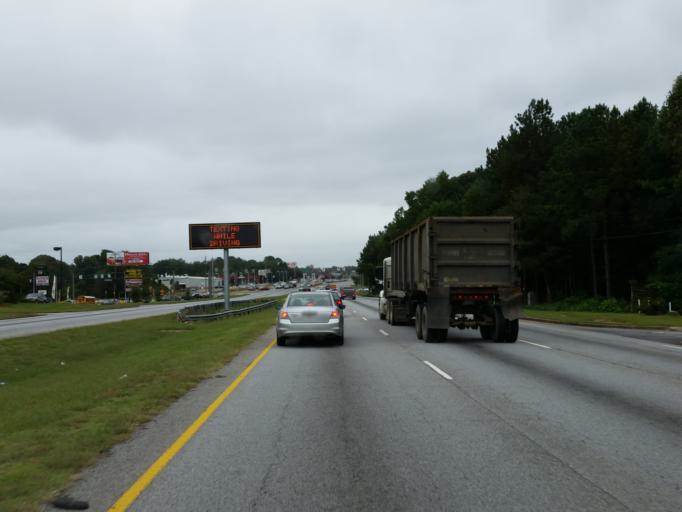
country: US
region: Georgia
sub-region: Clayton County
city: Morrow
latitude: 33.5811
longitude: -84.3761
